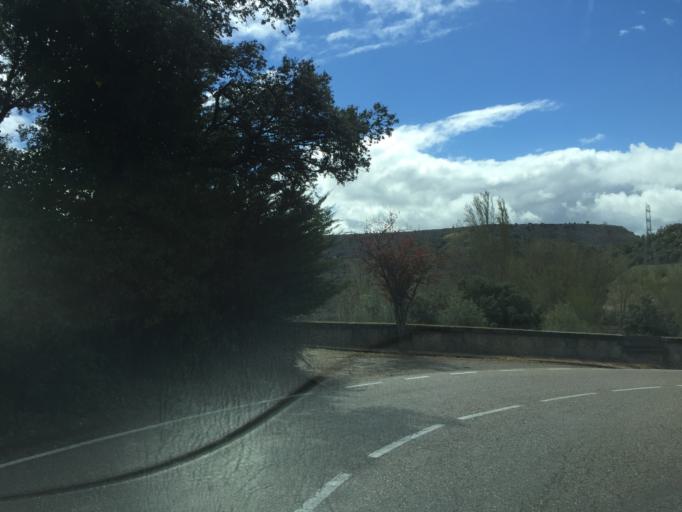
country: ES
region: Castille and Leon
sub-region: Provincia de Zamora
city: Moral de Sayago
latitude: 41.4939
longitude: -6.0859
